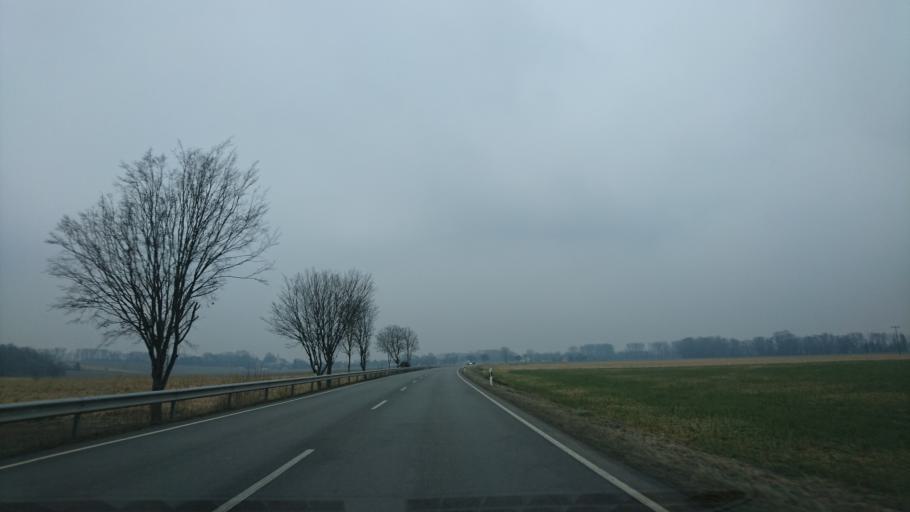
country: DE
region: Bavaria
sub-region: Lower Bavaria
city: Pocking
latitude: 48.4239
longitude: 13.3016
